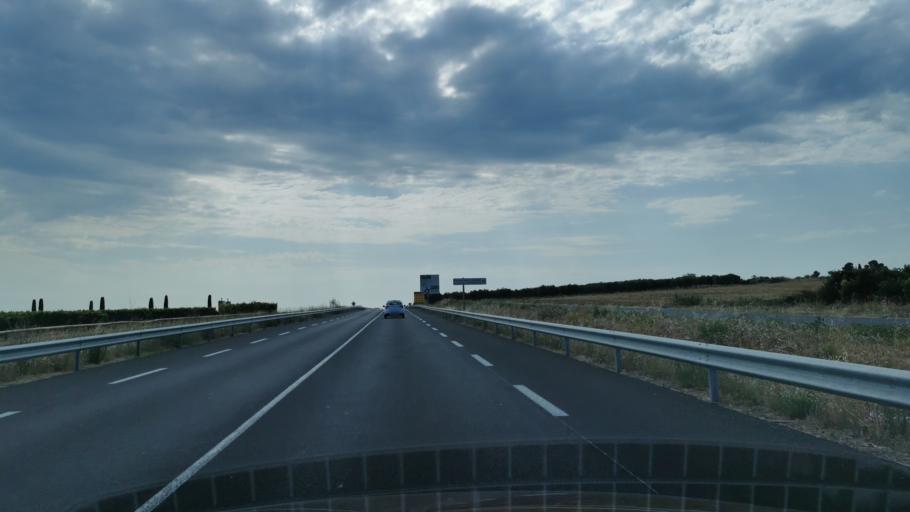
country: FR
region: Languedoc-Roussillon
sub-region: Departement de l'Herault
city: Puisserguier
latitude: 43.3662
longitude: 3.0652
